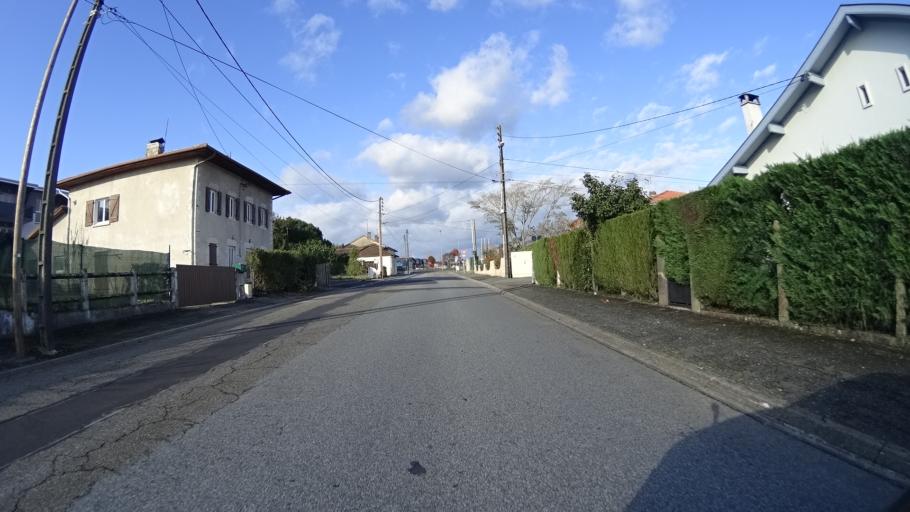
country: FR
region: Aquitaine
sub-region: Departement des Landes
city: Saint-Paul-les-Dax
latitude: 43.7260
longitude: -1.0837
